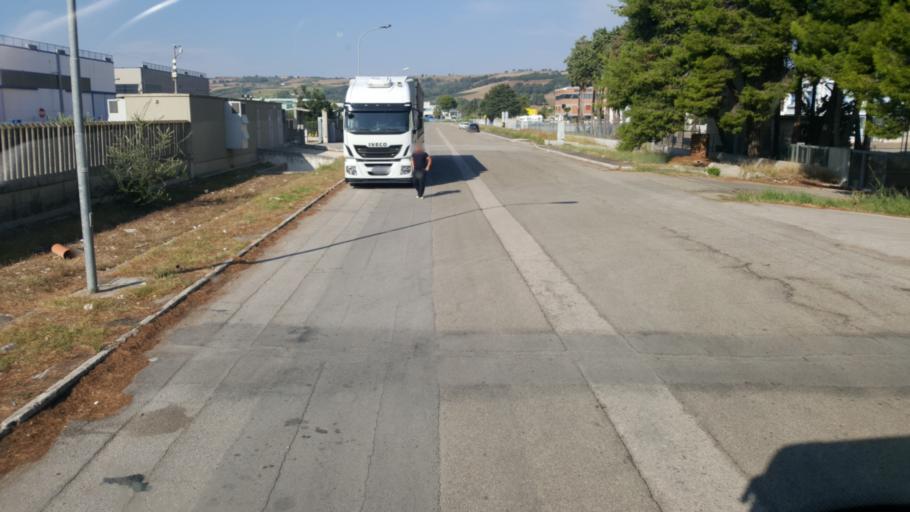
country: IT
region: Molise
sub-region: Provincia di Campobasso
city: Portocannone
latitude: 41.9448
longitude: 14.9974
